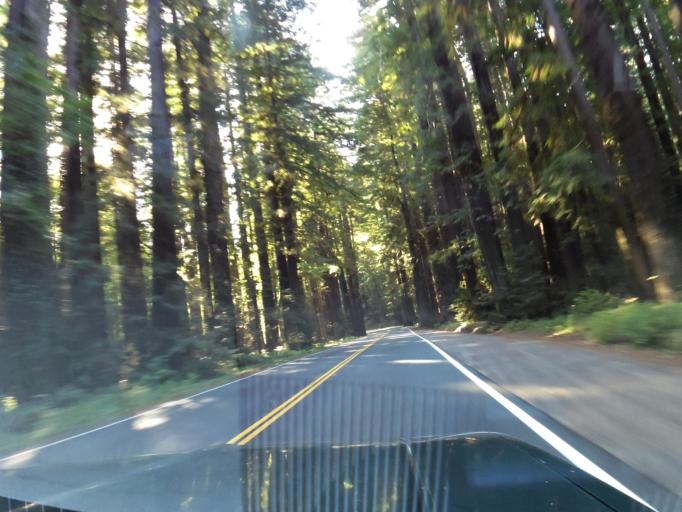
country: US
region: California
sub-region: Mendocino County
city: Boonville
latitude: 39.1554
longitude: -123.6232
